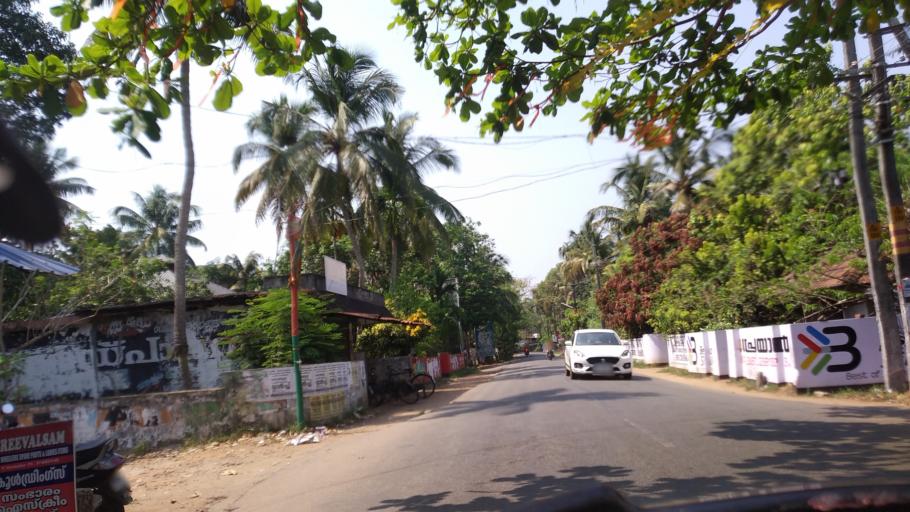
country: IN
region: Kerala
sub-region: Thrissur District
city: Kodungallur
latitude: 10.2731
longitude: 76.1397
